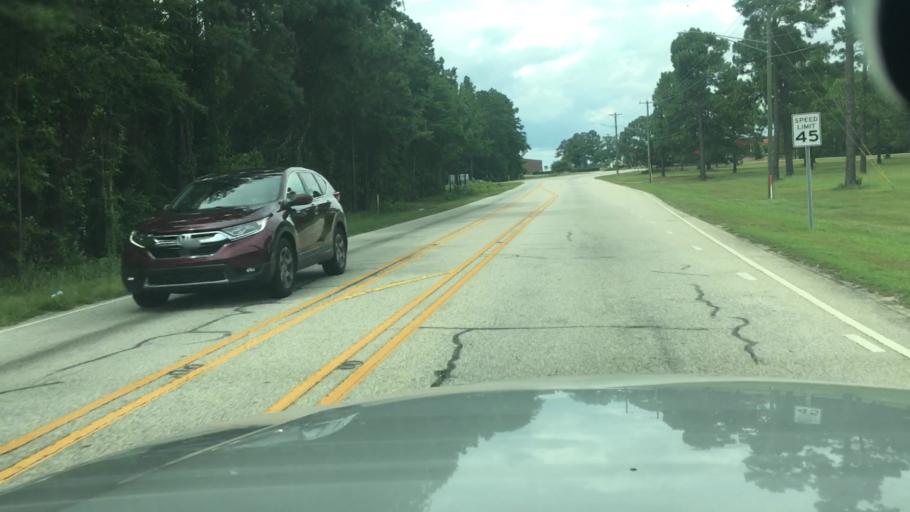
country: US
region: North Carolina
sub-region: Cumberland County
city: Hope Mills
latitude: 34.9941
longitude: -78.8914
